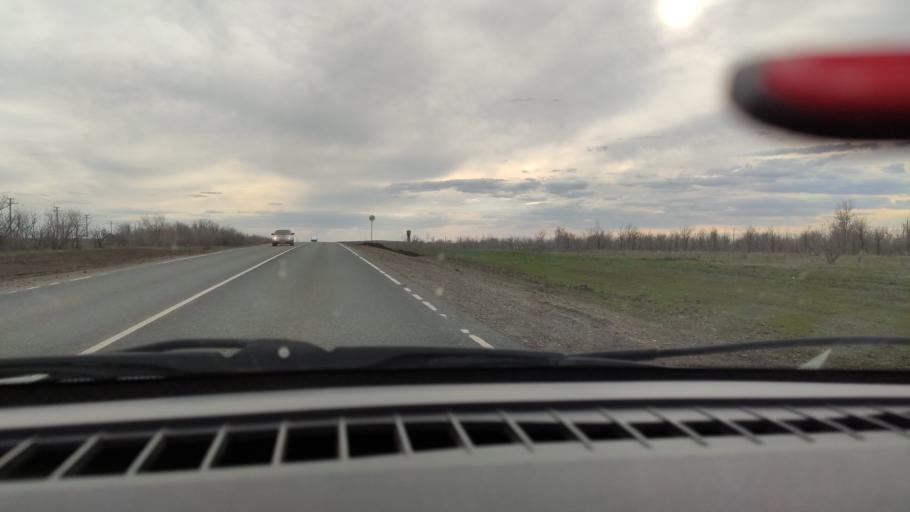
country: RU
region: Bashkortostan
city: Mayachnyy
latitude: 52.3415
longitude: 55.5339
